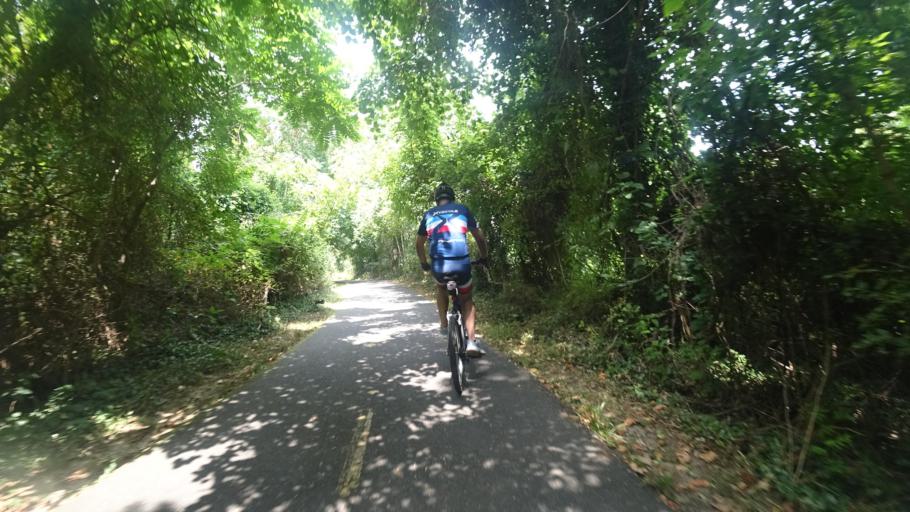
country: US
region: Virginia
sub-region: City of Alexandria
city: Alexandria
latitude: 38.8236
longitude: -77.0418
